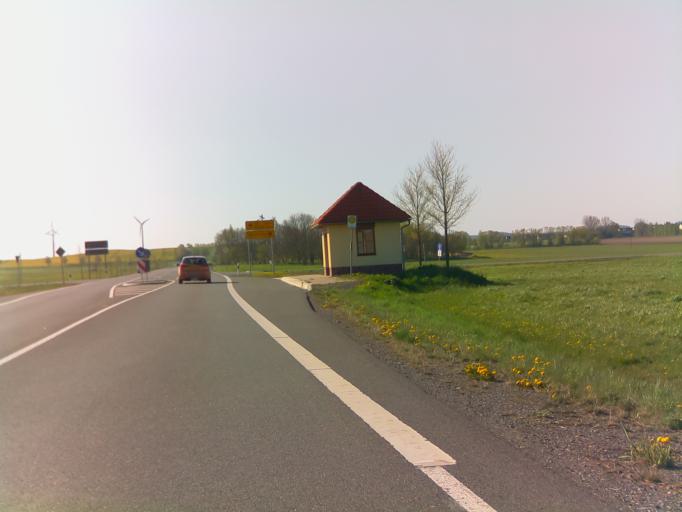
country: DE
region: Thuringia
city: Pormitz
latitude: 50.6172
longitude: 11.8203
